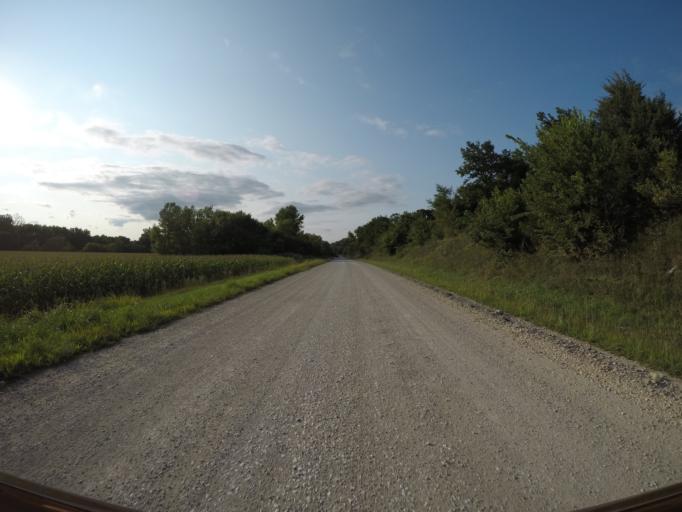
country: US
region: Kansas
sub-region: Wabaunsee County
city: Alma
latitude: 38.9735
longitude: -96.2631
